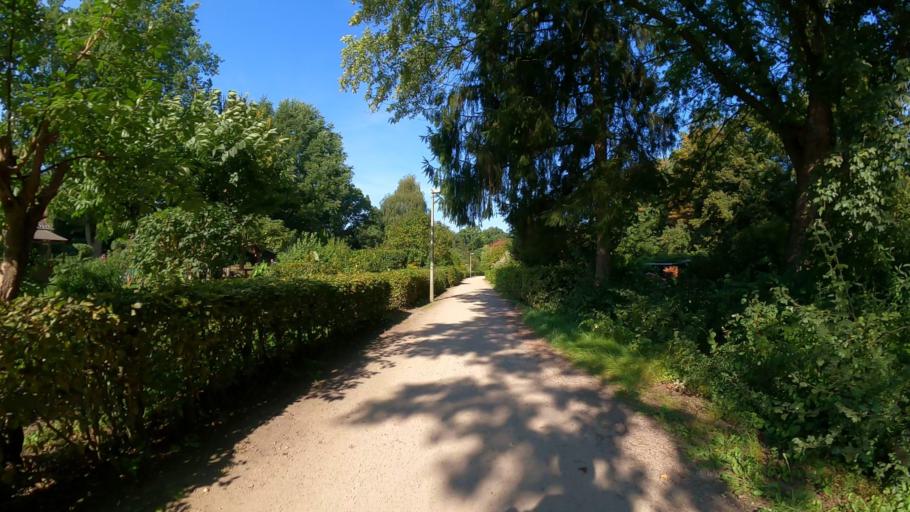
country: DE
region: Hamburg
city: Fuhlsbuettel
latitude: 53.6357
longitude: 10.0199
